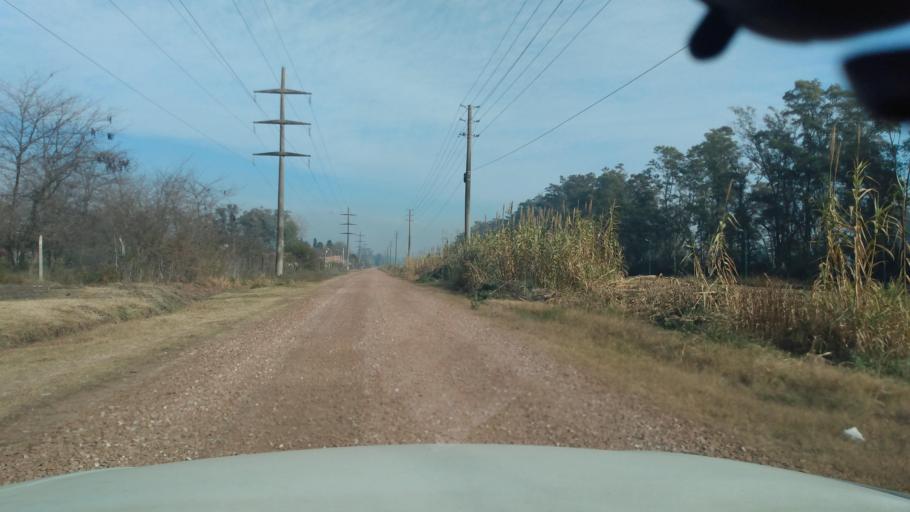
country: AR
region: Buenos Aires
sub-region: Partido de Lujan
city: Lujan
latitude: -34.5861
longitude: -59.1294
